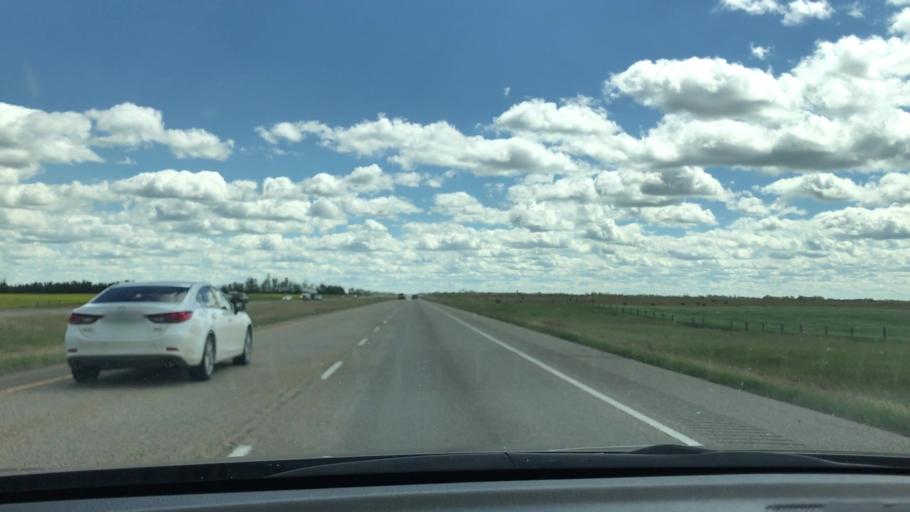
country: CA
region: Alberta
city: Leduc
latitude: 53.1629
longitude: -113.5983
